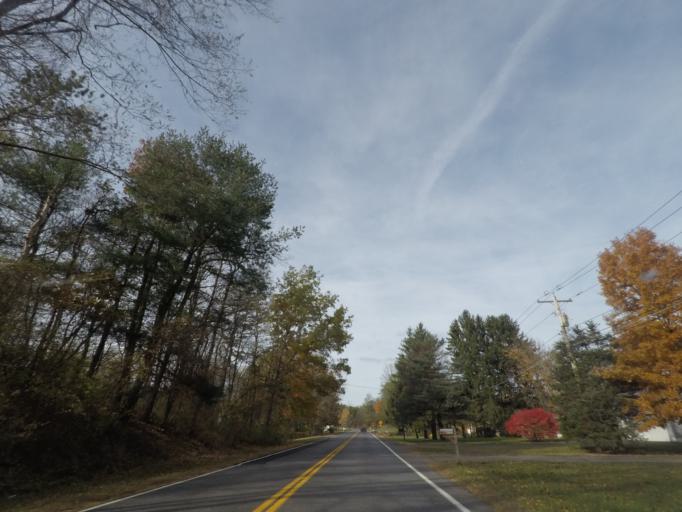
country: US
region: New York
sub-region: Albany County
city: Westmere
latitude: 42.7240
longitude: -73.8846
